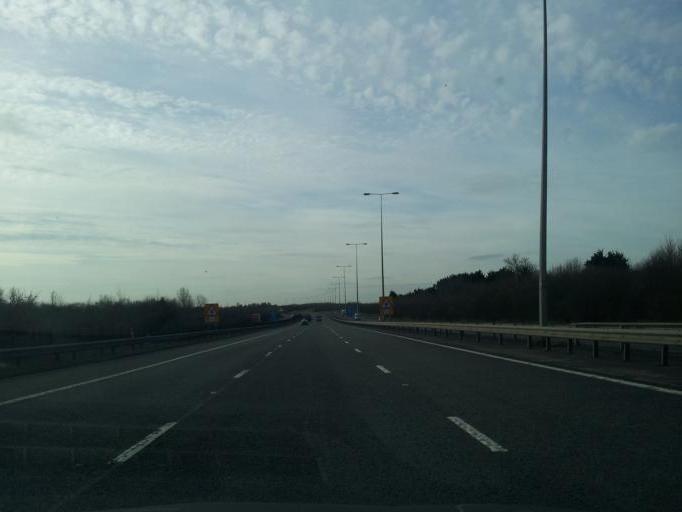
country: GB
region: England
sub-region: Cambridgeshire
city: Great Stukeley
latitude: 52.3692
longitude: -0.2532
